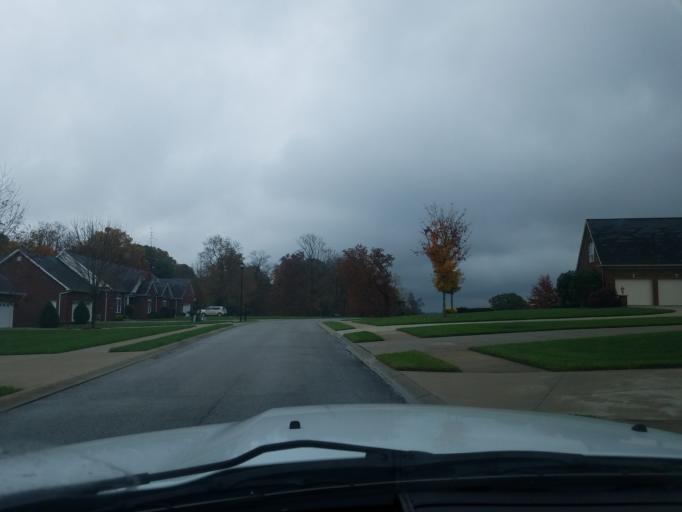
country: US
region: Kentucky
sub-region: Taylor County
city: Campbellsville
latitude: 37.3630
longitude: -85.3797
